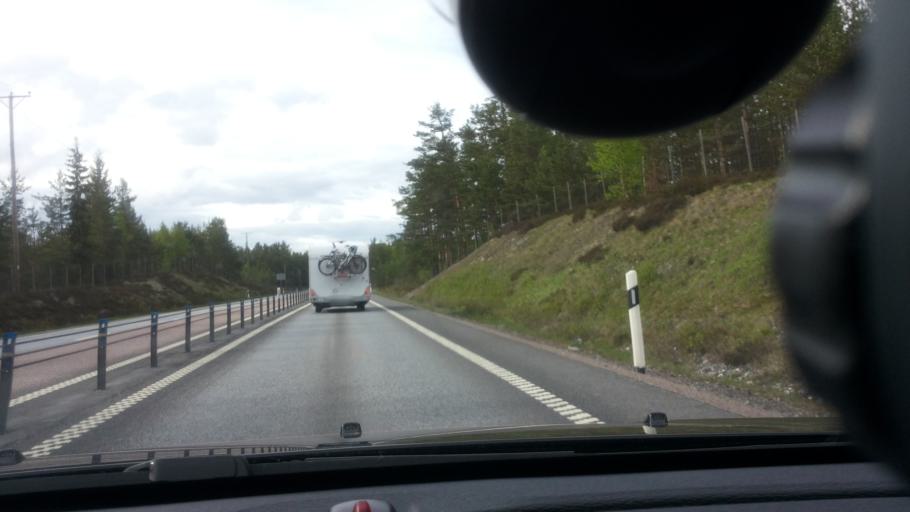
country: SE
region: Gaevleborg
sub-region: Gavle Kommun
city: Norrsundet
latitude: 61.0156
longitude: 16.9792
